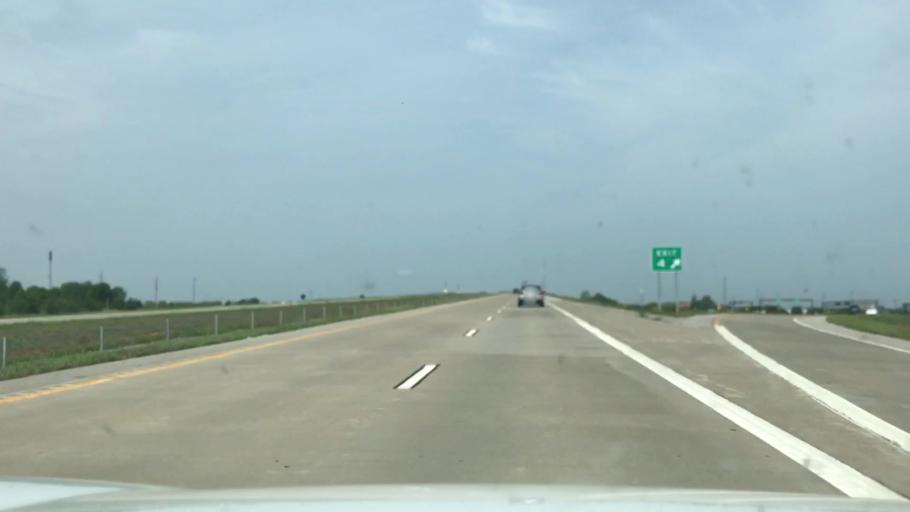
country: US
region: Missouri
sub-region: Saint Charles County
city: Dardenne Prairie
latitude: 38.7524
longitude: -90.6962
